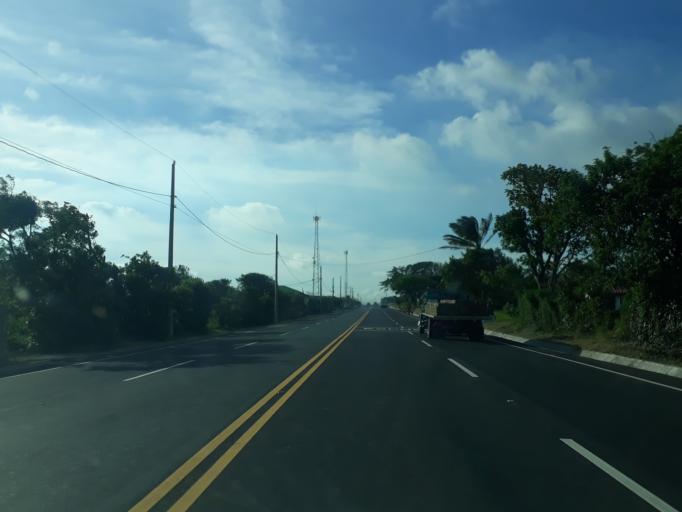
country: NI
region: Managua
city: El Crucero
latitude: 11.9224
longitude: -86.2805
